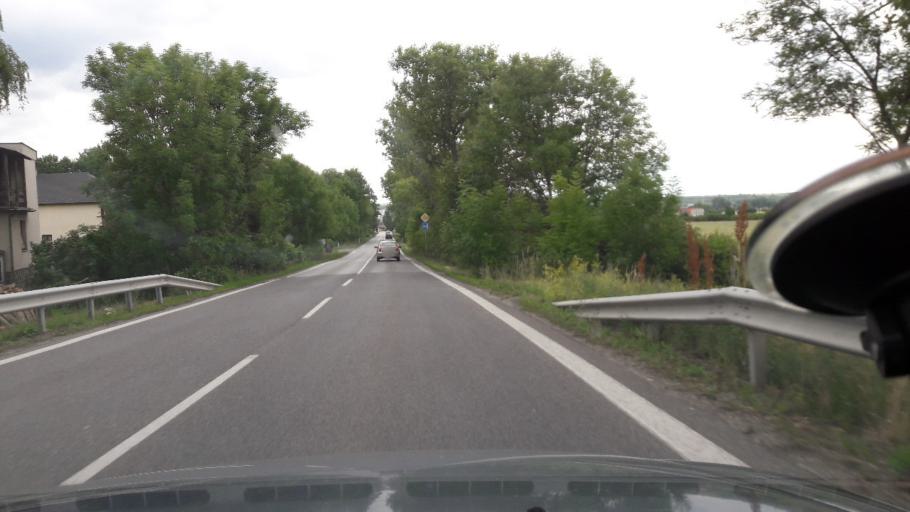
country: SK
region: Bratislavsky
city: Modra
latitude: 48.3097
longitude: 17.2939
